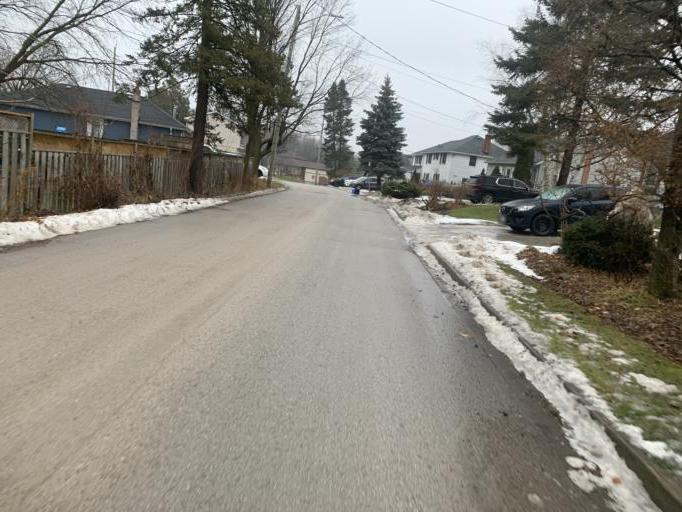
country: CA
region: Ontario
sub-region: Halton
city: Milton
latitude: 43.6581
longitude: -79.9267
